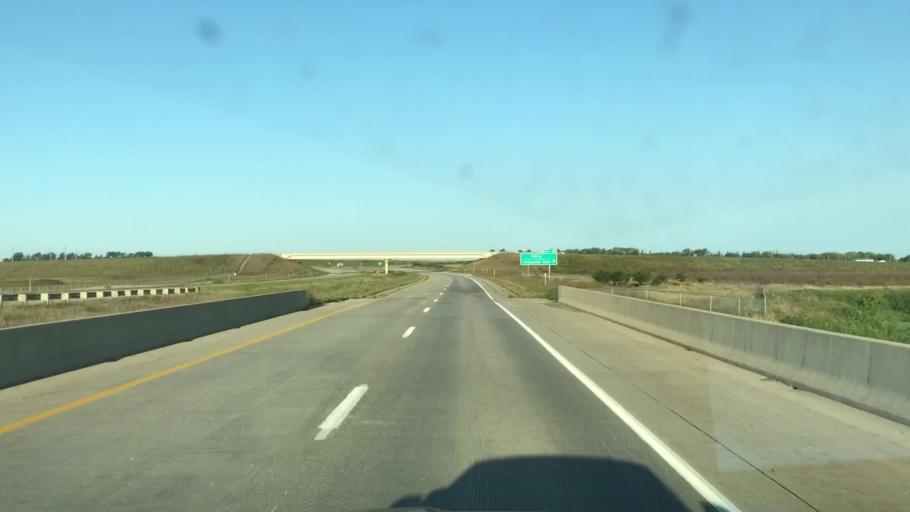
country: US
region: Iowa
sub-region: Osceola County
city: Sibley
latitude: 43.3845
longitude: -95.7376
